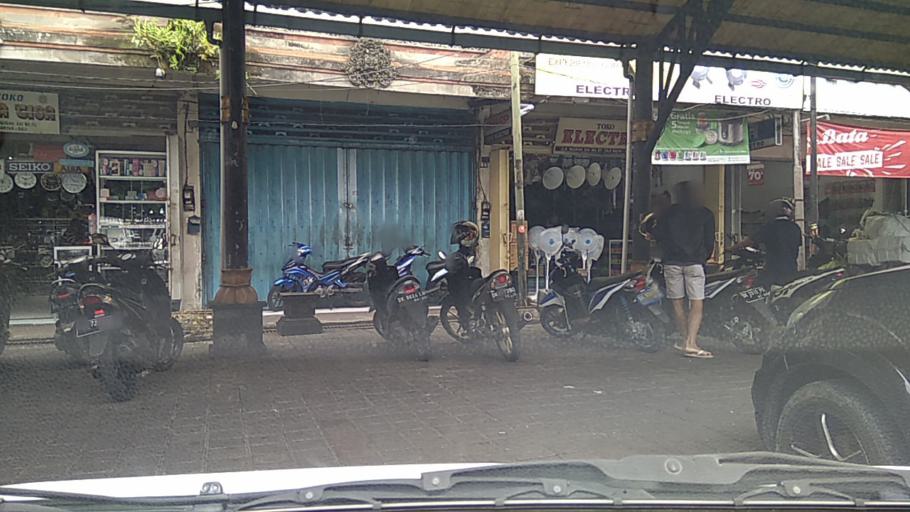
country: ID
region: Bali
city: Banjar Kelodan
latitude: -8.5414
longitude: 115.3270
